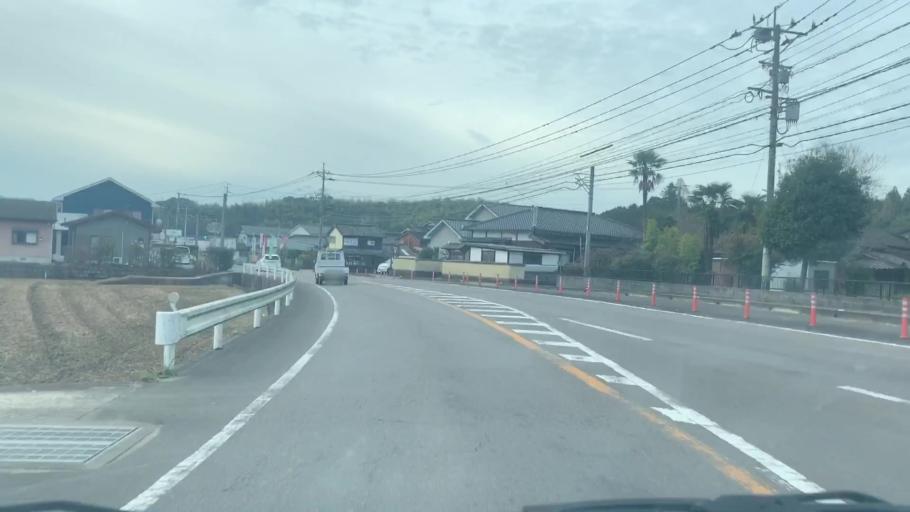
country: JP
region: Saga Prefecture
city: Kashima
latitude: 33.1493
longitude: 130.0633
